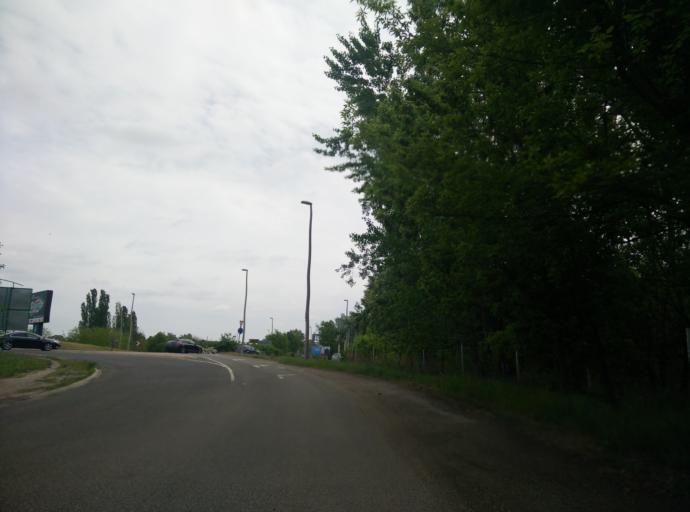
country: HU
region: Pest
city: Dunakeszi
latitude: 47.6054
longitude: 19.1100
